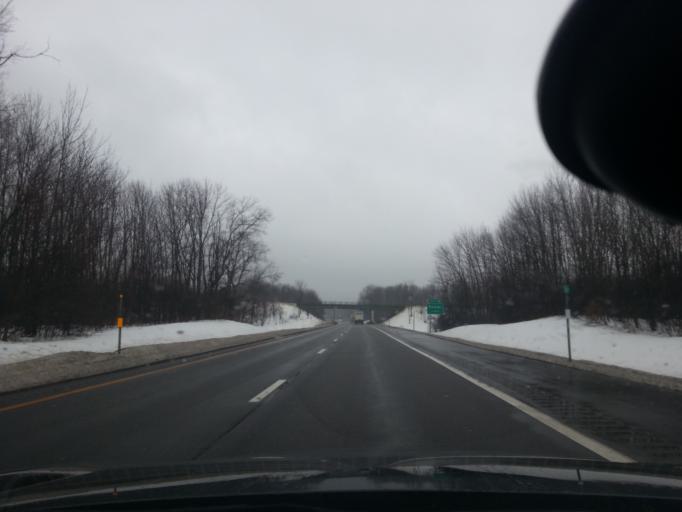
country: US
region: New York
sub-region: Oswego County
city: Pulaski
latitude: 43.5879
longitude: -76.1081
